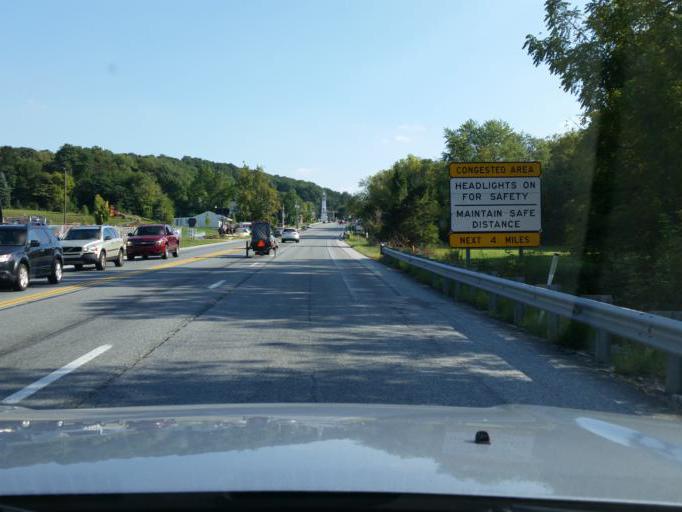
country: US
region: Pennsylvania
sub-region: Lancaster County
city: Gap
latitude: 39.9893
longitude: -76.0200
